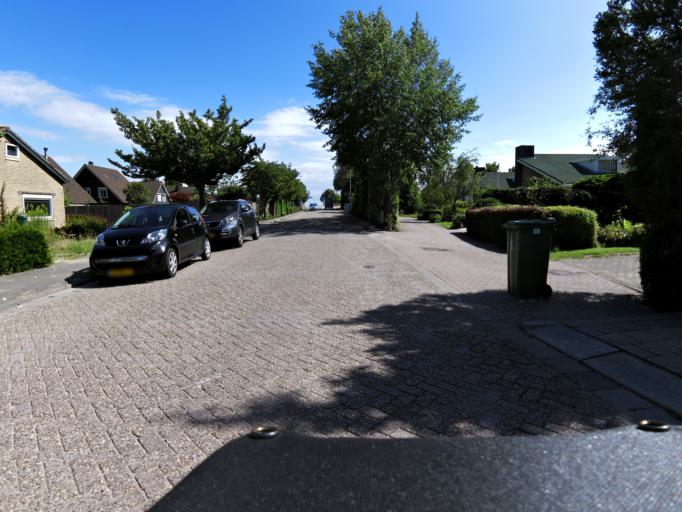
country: NL
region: South Holland
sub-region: Gemeente Goeree-Overflakkee
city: Dirksland
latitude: 51.7653
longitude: 4.0709
